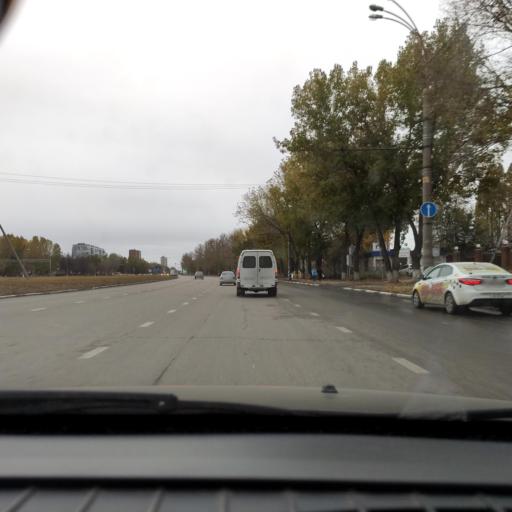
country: RU
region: Samara
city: Tol'yatti
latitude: 53.5225
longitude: 49.2590
